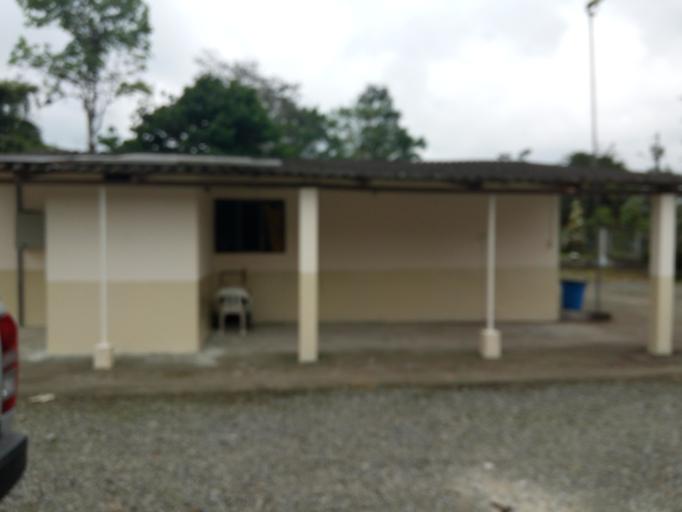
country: EC
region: Santo Domingo de los Tsachilas
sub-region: Canton Santo Domingo de los Colorados
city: Santo Domingo de los Colorados
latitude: -0.2224
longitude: -79.2597
